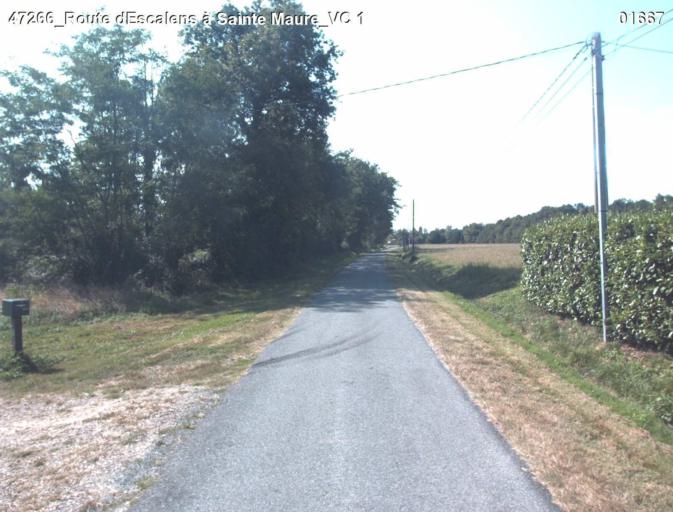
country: FR
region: Aquitaine
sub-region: Departement des Landes
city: Gabarret
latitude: 44.0093
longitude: 0.0766
